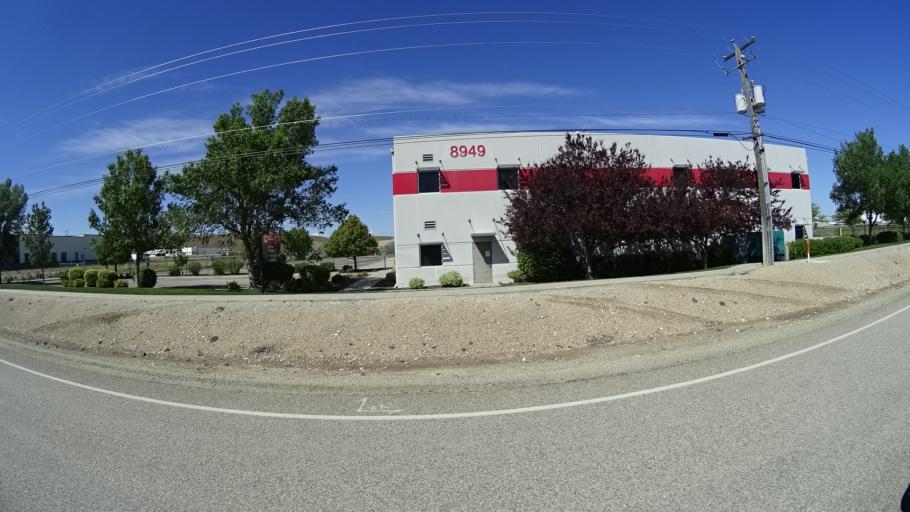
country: US
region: Idaho
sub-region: Ada County
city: Boise
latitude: 43.5208
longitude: -116.1467
